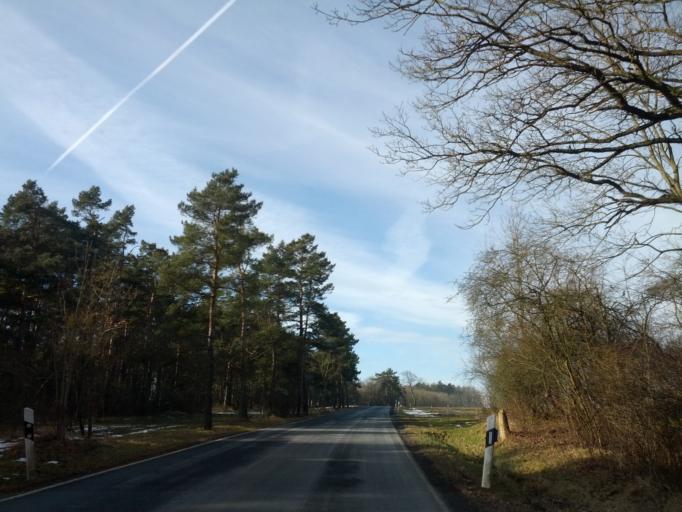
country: DE
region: Thuringia
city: Weberstedt
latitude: 51.0508
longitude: 10.5014
